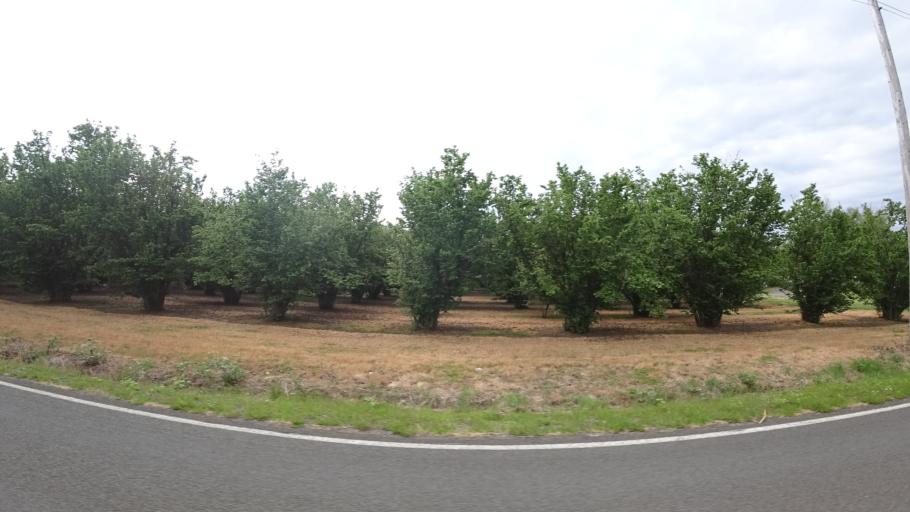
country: US
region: Oregon
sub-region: Washington County
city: Hillsboro
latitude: 45.4774
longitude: -122.9534
